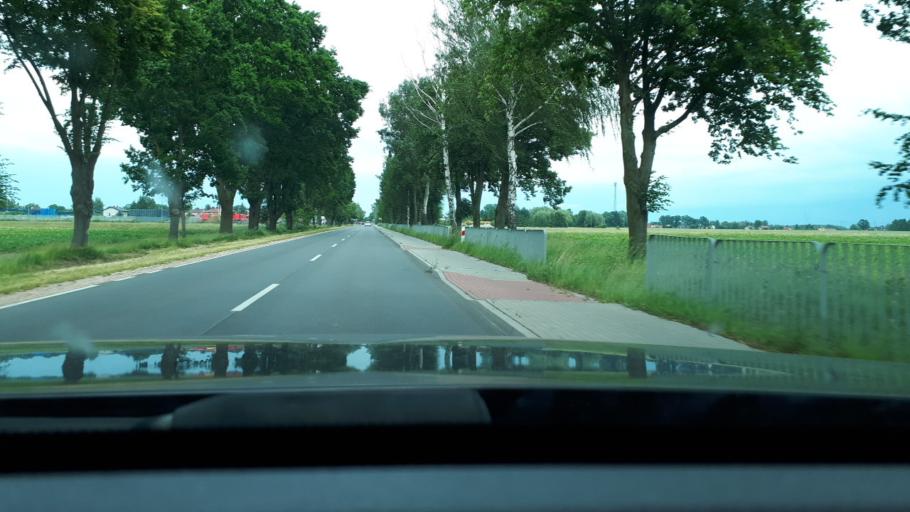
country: PL
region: Masovian Voivodeship
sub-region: Powiat warszawski zachodni
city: Kampinos
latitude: 52.2691
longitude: 20.4479
